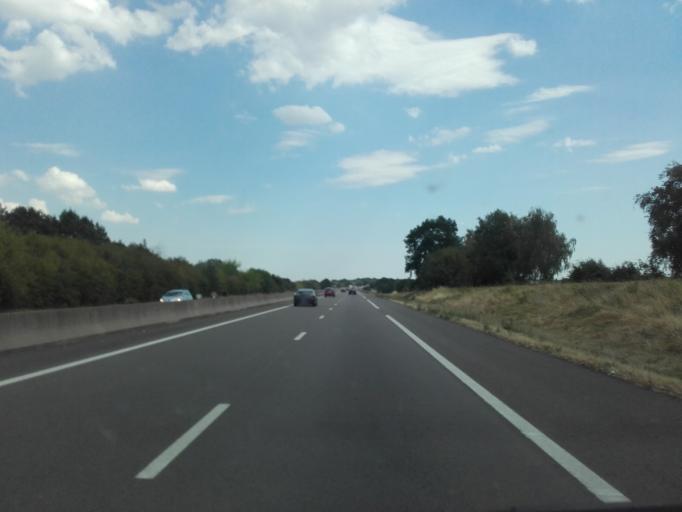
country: FR
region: Bourgogne
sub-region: Departement de la Cote-d'Or
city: Semur-en-Auxois
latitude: 47.4697
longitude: 4.2280
